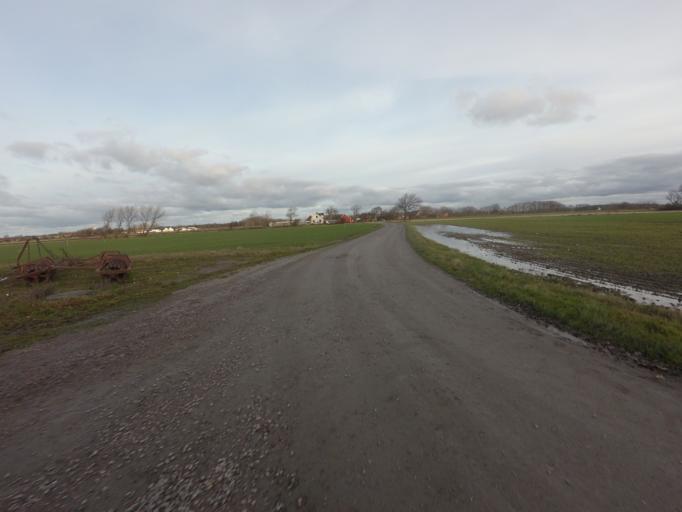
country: SE
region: Skane
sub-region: Hoganas Kommun
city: Hoganas
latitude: 56.1681
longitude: 12.5805
